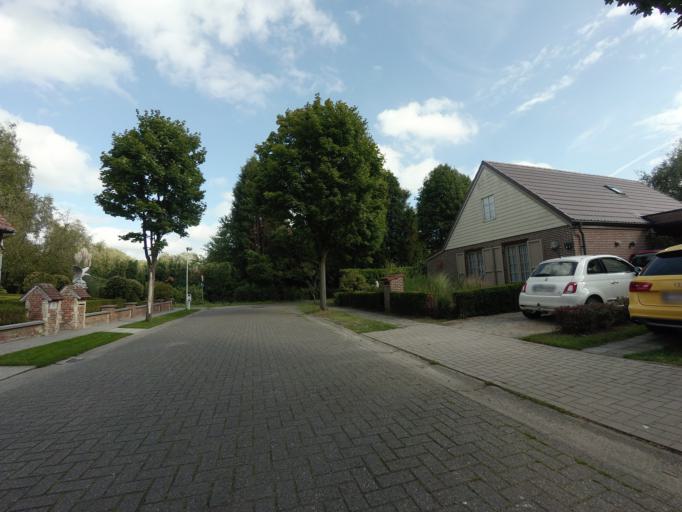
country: BE
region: Flanders
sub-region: Provincie Antwerpen
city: Aartselaar
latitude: 51.1088
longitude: 4.3949
